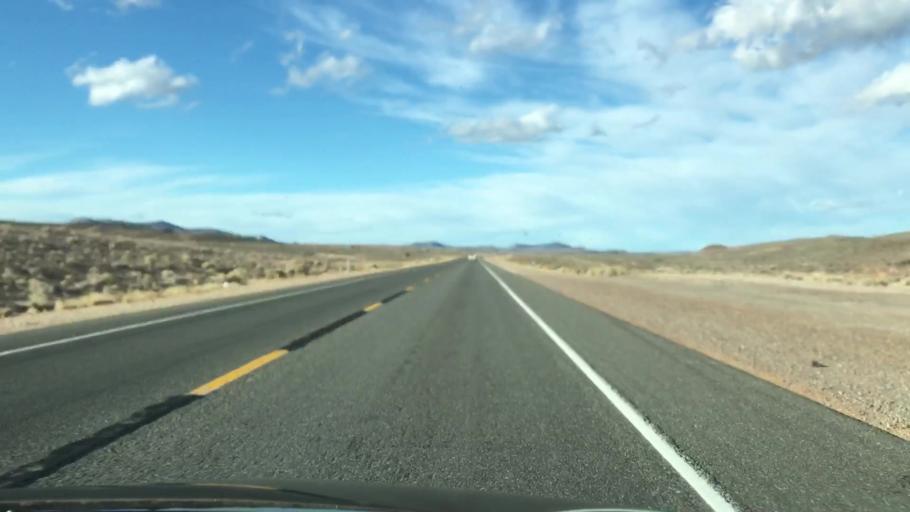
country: US
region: Nevada
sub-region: Esmeralda County
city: Goldfield
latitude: 37.5373
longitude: -117.1942
